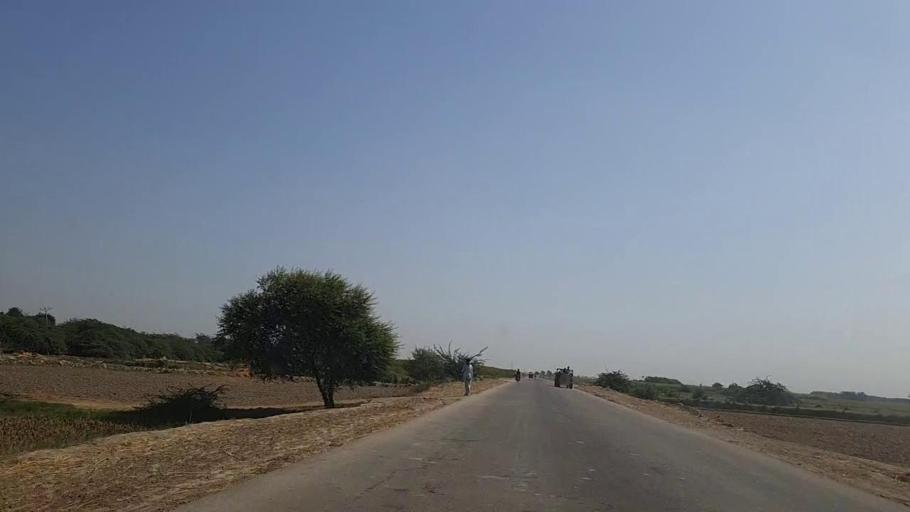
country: PK
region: Sindh
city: Mirpur Batoro
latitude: 24.7563
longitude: 68.2275
